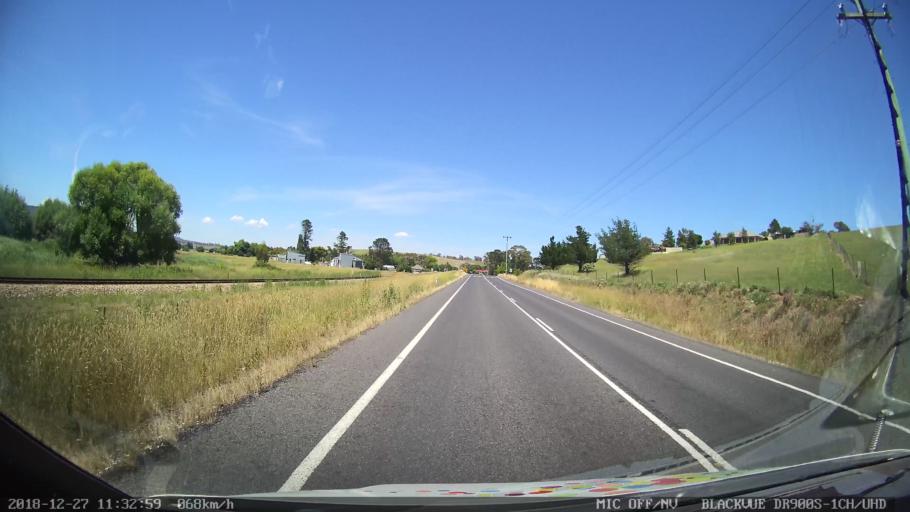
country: AU
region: New South Wales
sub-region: Bathurst Regional
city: Perthville
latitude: -33.5117
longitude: 149.5277
